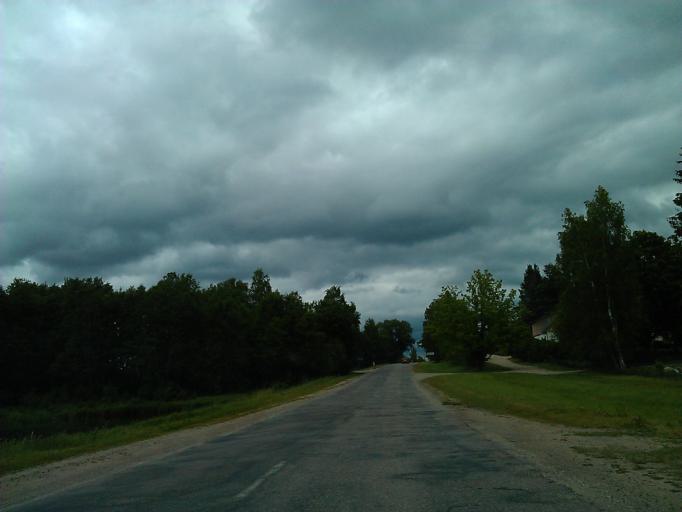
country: LV
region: Kuldigas Rajons
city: Kuldiga
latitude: 56.9601
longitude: 21.9474
